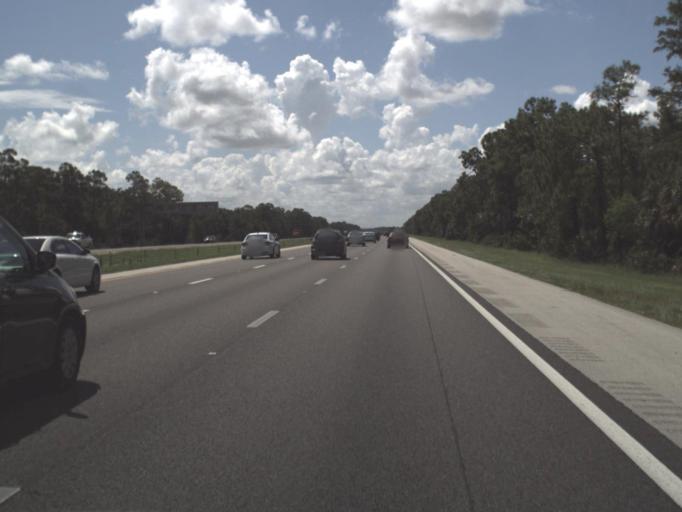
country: US
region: Florida
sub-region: Lee County
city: Three Oaks
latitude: 26.4686
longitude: -81.7900
